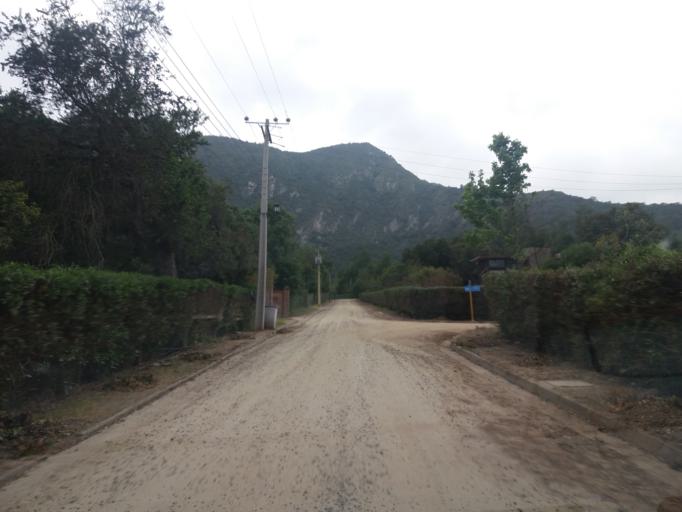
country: CL
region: Valparaiso
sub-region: Provincia de Marga Marga
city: Limache
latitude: -33.0237
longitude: -71.1371
